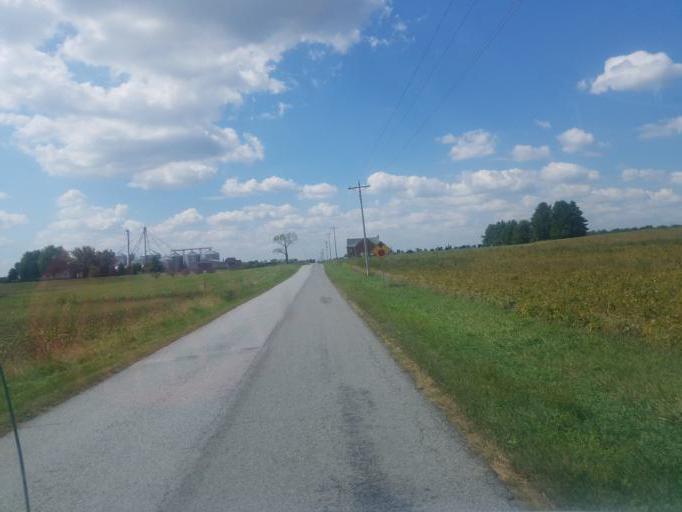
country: US
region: Ohio
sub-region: Hardin County
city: Ada
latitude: 40.6520
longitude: -83.9157
